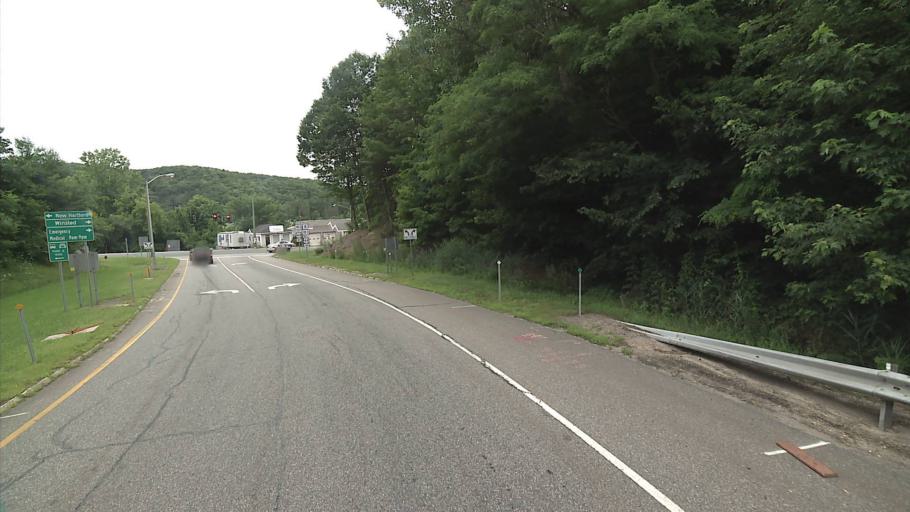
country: US
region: Connecticut
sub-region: Litchfield County
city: Winsted
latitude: 41.9170
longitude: -73.0554
